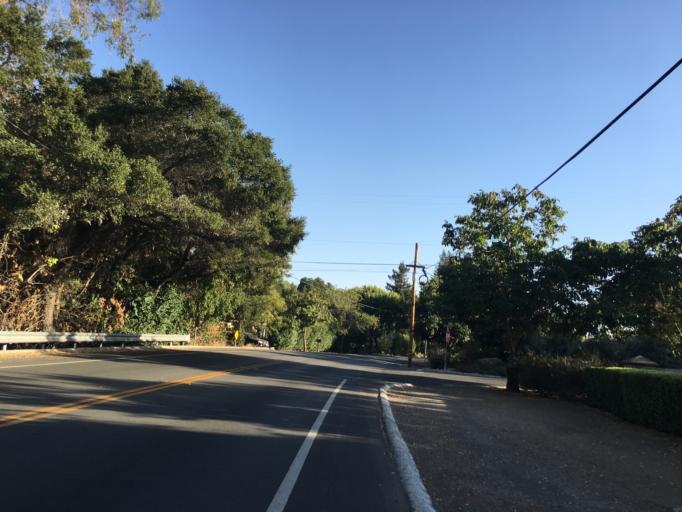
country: US
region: California
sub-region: Santa Clara County
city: Loyola
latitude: 37.3579
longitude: -122.0871
